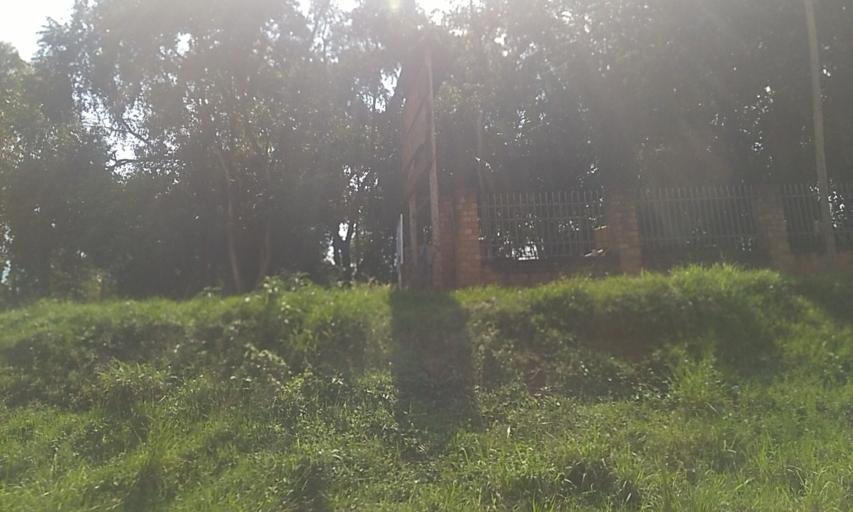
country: UG
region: Central Region
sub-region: Wakiso District
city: Kireka
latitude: 0.3635
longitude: 32.6063
